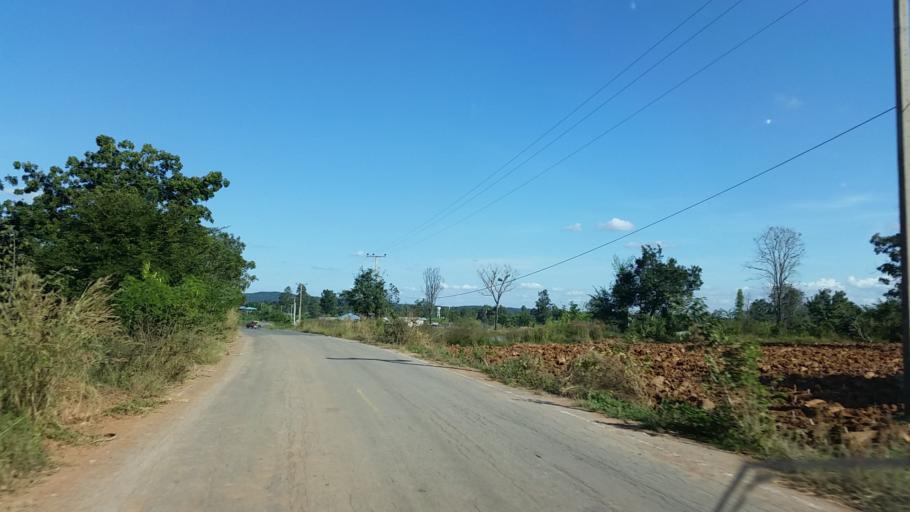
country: TH
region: Chaiyaphum
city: Thep Sathit
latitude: 15.5460
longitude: 101.4649
